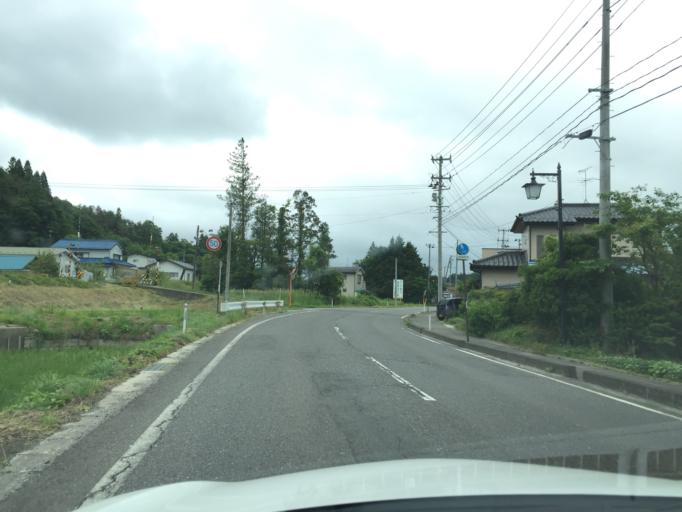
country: JP
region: Fukushima
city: Funehikimachi-funehiki
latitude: 37.4136
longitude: 140.6094
